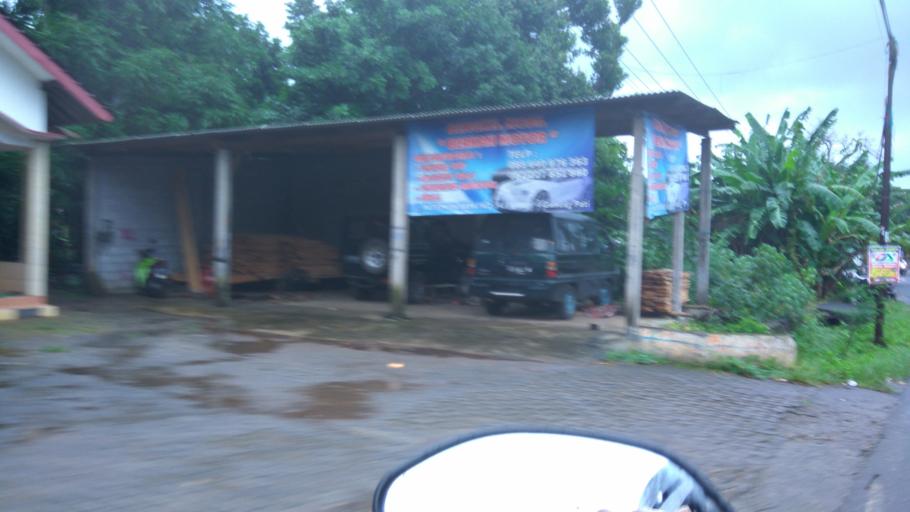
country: ID
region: Central Java
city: Semarang
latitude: -7.0625
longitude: 110.3967
